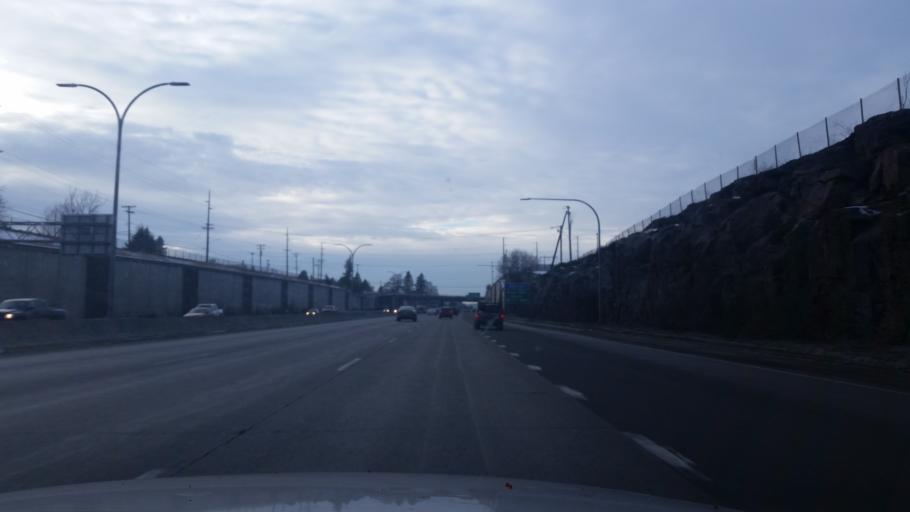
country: US
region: Washington
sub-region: Spokane County
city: Spokane
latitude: 47.6524
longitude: -117.3980
